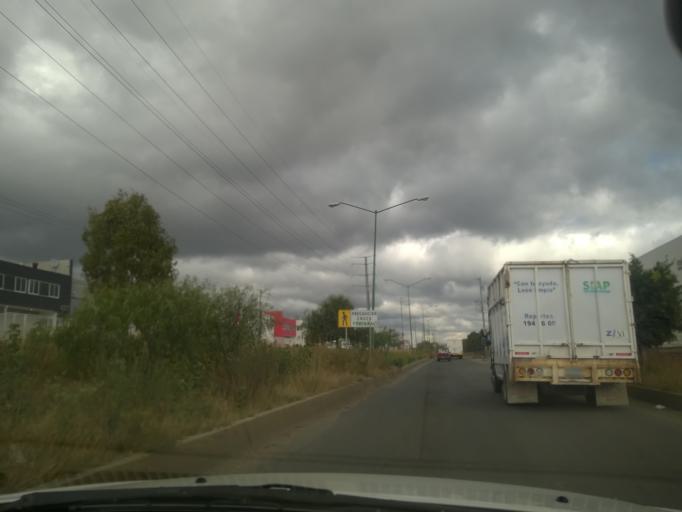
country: MX
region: Guanajuato
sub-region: Leon
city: La Ermita
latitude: 21.1574
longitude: -101.7315
